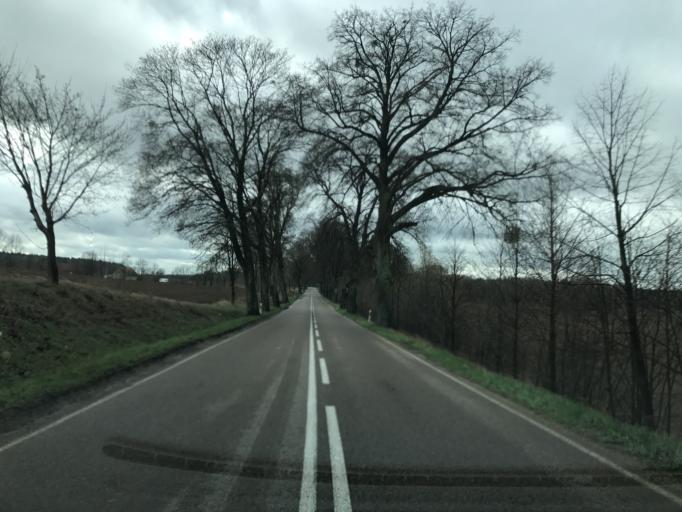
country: PL
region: Warmian-Masurian Voivodeship
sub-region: Powiat olsztynski
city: Olsztynek
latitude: 53.5314
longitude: 20.2532
